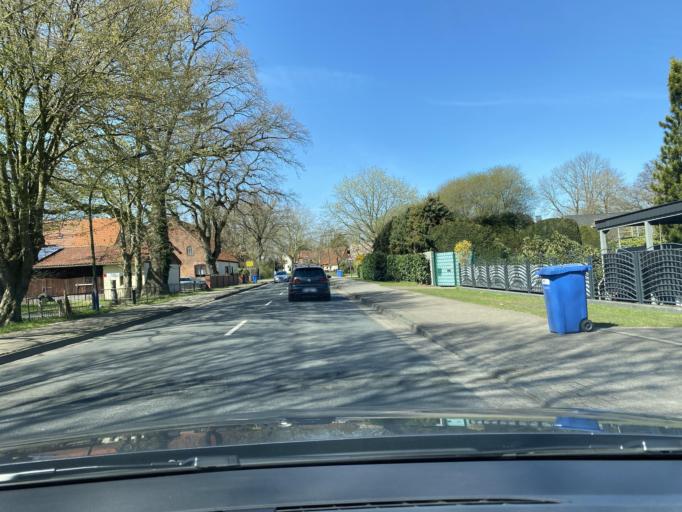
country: DE
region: Lower Saxony
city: Oyten
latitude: 53.0724
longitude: 9.0195
